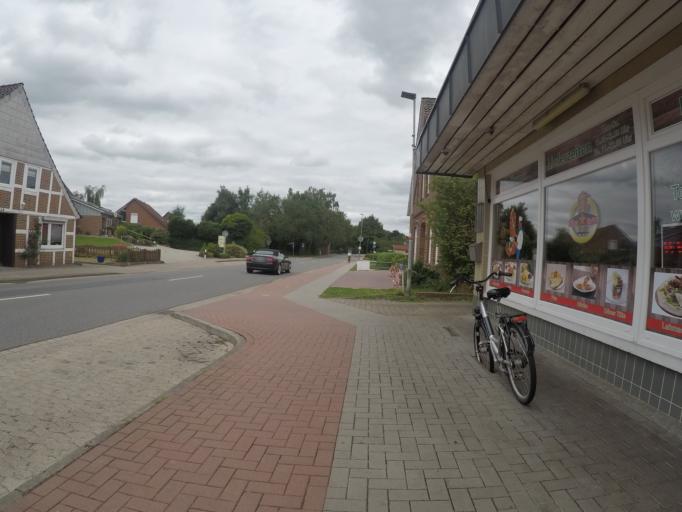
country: DE
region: Lower Saxony
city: Himmelpforten
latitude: 53.6172
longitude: 9.3062
